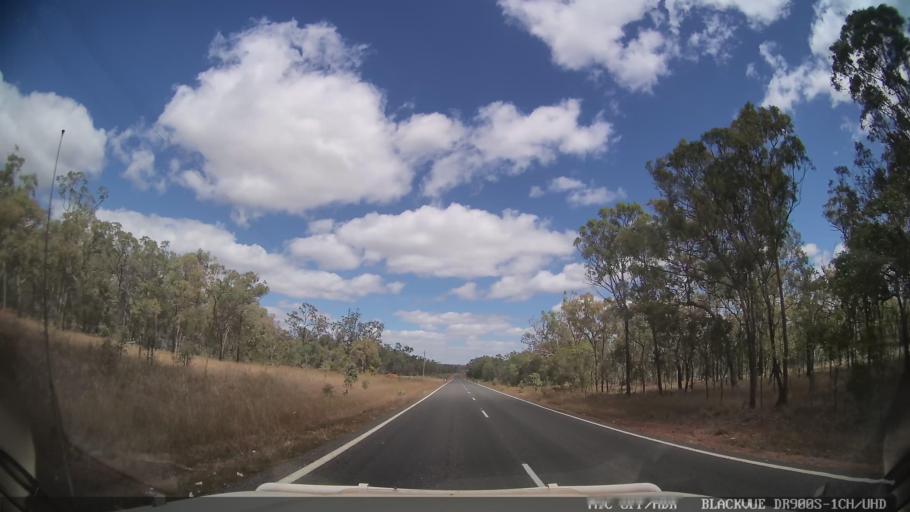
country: AU
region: Queensland
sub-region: Tablelands
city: Ravenshoe
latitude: -18.0274
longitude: 144.8701
